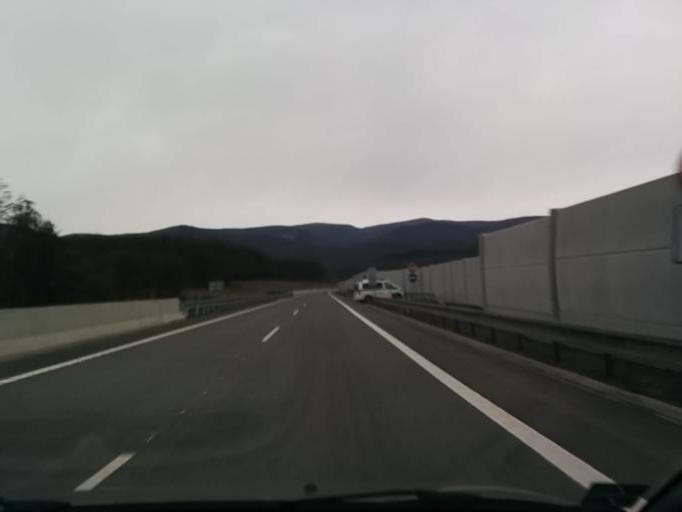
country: SK
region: Nitriansky
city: Tlmace
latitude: 48.3634
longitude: 18.4999
